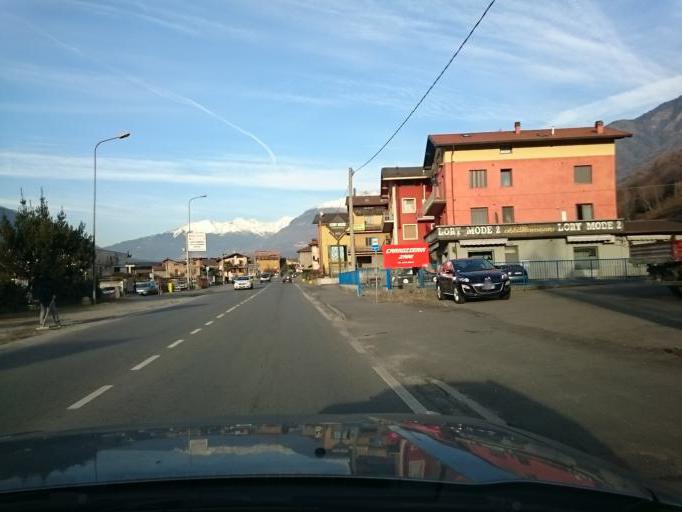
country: IT
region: Lombardy
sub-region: Provincia di Brescia
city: Breno
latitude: 45.9651
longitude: 10.3162
